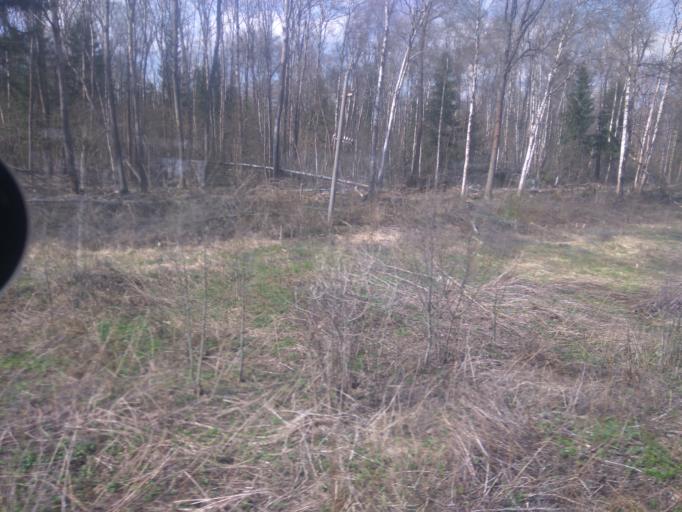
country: RU
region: Moskovskaya
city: Dmitrov
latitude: 56.2962
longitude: 37.5939
